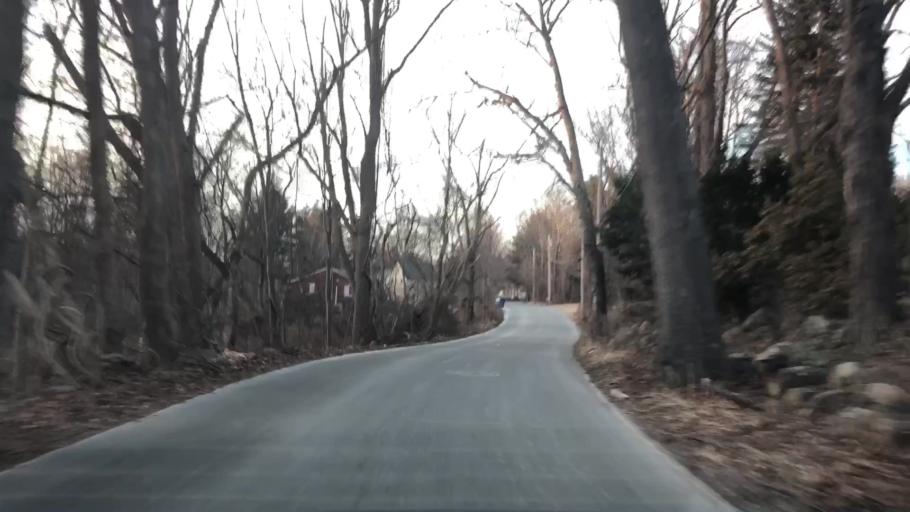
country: US
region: Massachusetts
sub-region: Essex County
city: North Andover
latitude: 42.6986
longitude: -71.0765
